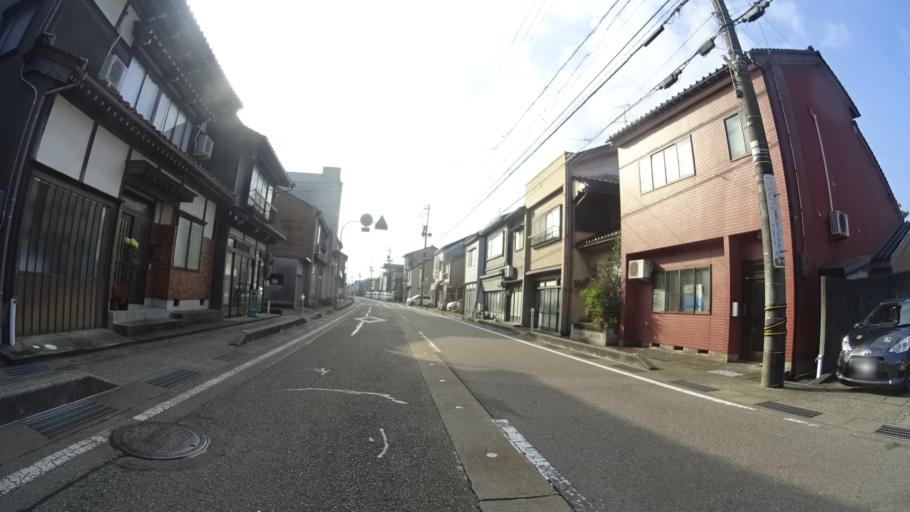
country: JP
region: Toyama
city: Himi
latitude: 36.8686
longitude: 136.9832
